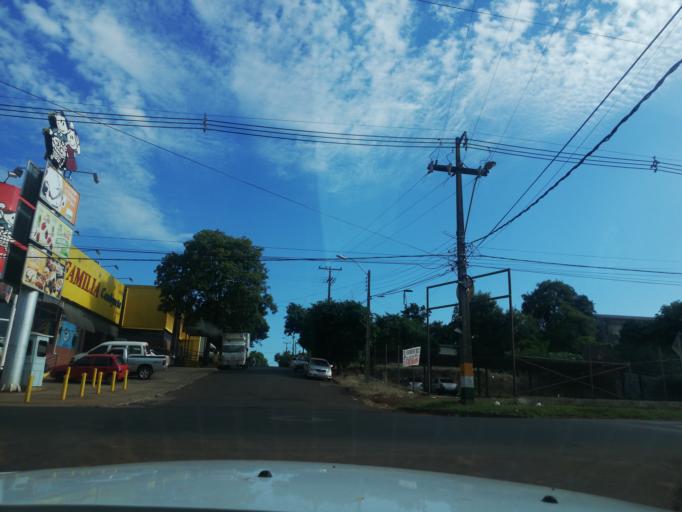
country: PY
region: Itapua
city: Encarnacion
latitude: -27.3430
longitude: -55.8477
